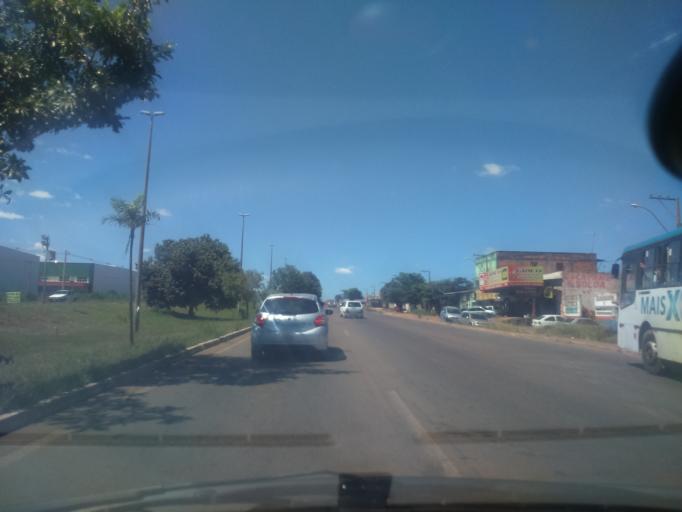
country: BR
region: Goias
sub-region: Luziania
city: Luziania
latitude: -16.0492
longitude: -48.0074
